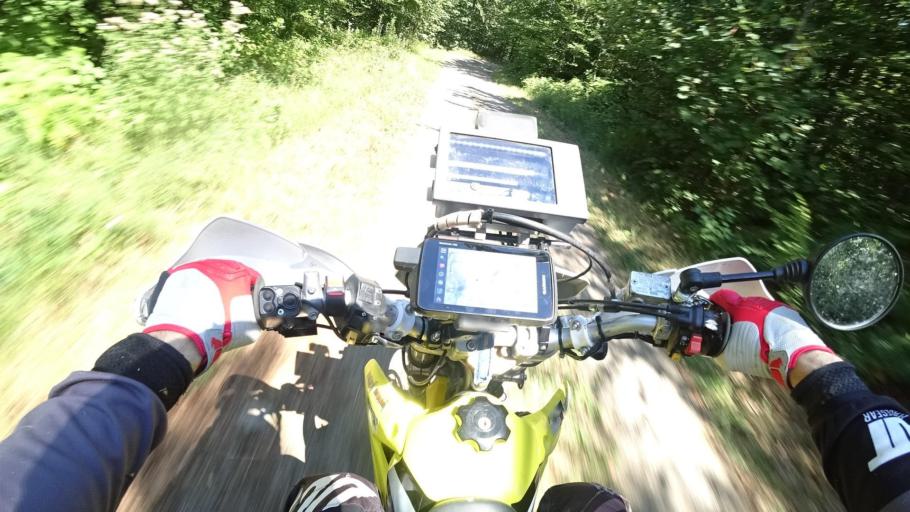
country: HR
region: Karlovacka
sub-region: Grad Ogulin
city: Ogulin
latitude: 45.2391
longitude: 15.1981
